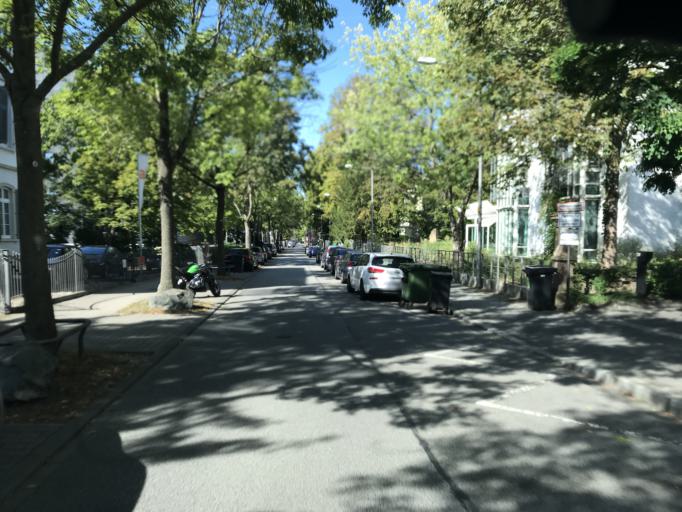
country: DE
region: Hesse
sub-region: Regierungsbezirk Darmstadt
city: Wiesbaden
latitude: 50.0766
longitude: 8.2480
